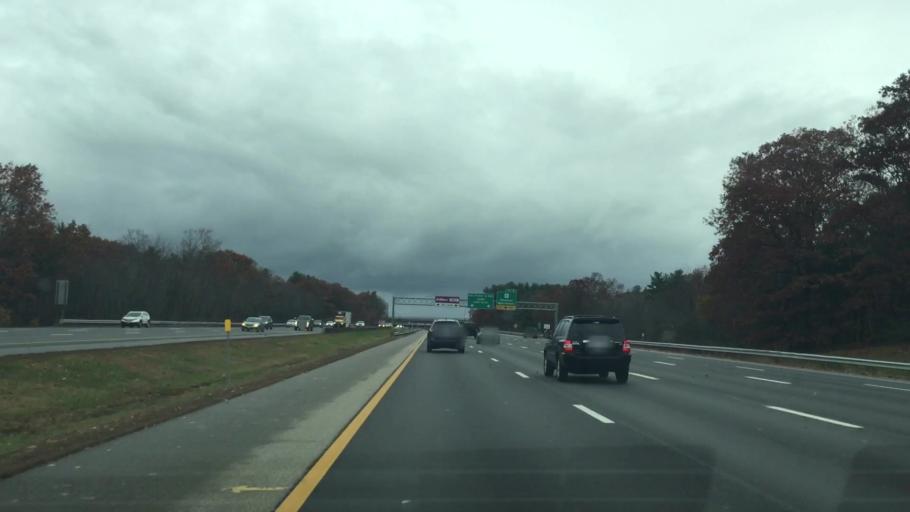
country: US
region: New Hampshire
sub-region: Rockingham County
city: Hampton
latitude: 42.9493
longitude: -70.8589
